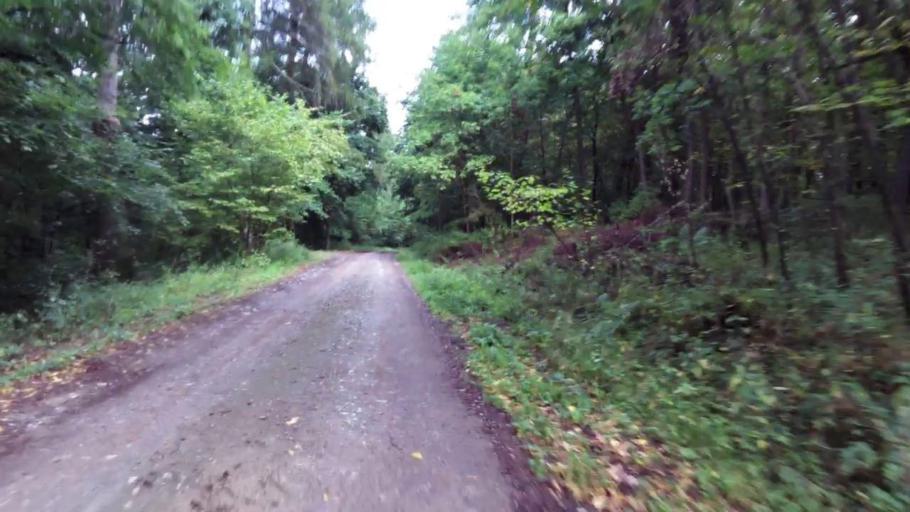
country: PL
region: West Pomeranian Voivodeship
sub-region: Powiat mysliborski
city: Debno
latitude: 52.8552
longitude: 14.6997
